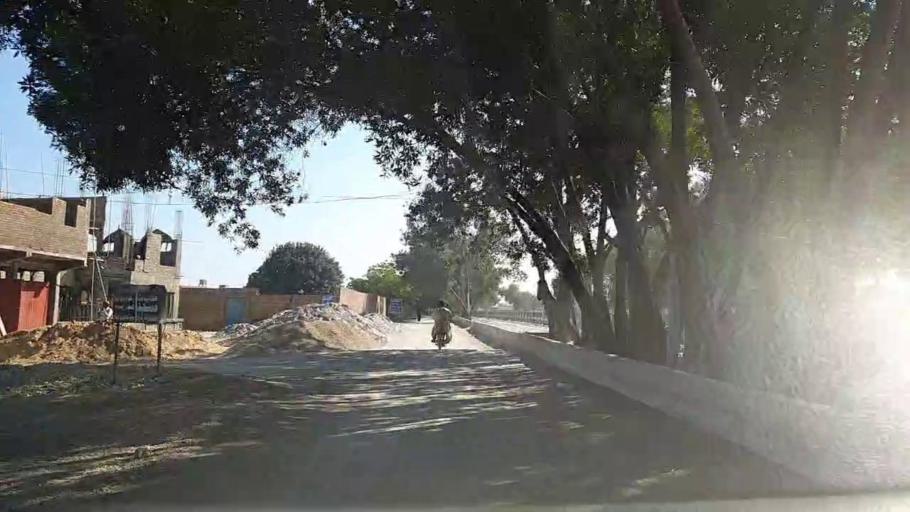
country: PK
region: Sindh
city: Nawabshah
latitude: 26.2473
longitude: 68.4212
